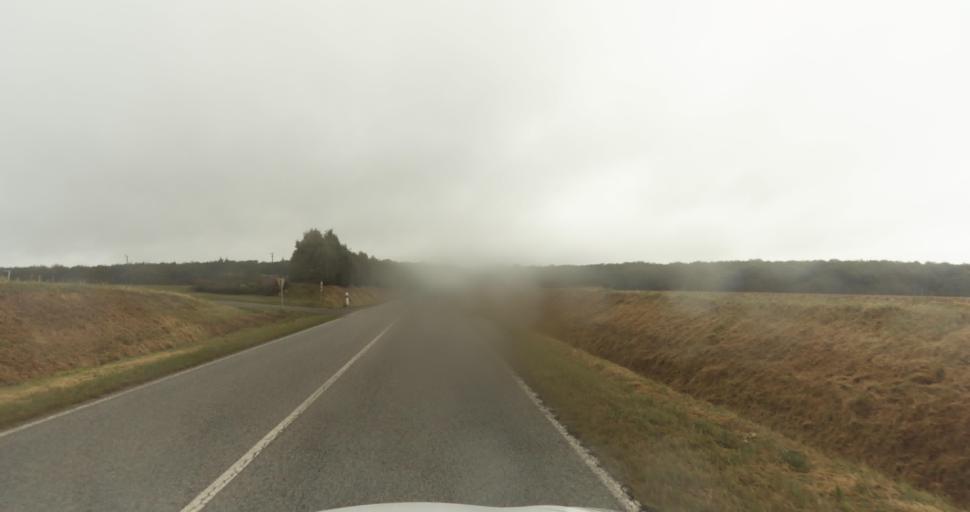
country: FR
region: Haute-Normandie
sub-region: Departement de l'Eure
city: Normanville
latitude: 49.1094
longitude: 1.1727
